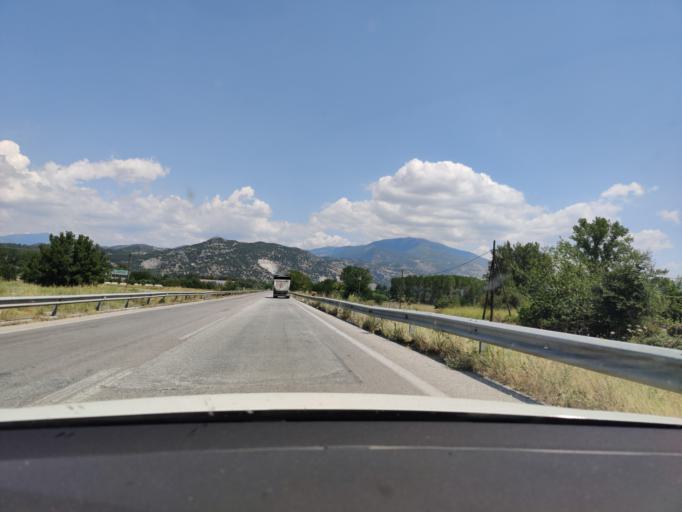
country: GR
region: Central Macedonia
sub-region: Nomos Serron
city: Serres
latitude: 41.0811
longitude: 23.5721
